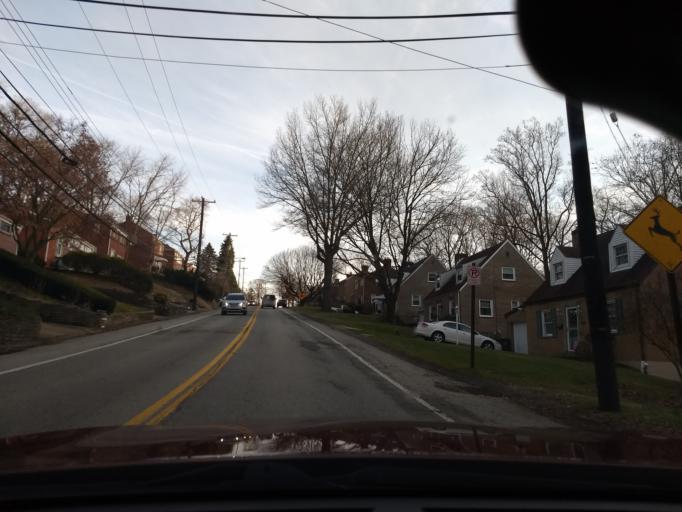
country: US
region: Pennsylvania
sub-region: Allegheny County
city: Brentwood
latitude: 40.3652
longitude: -79.9704
